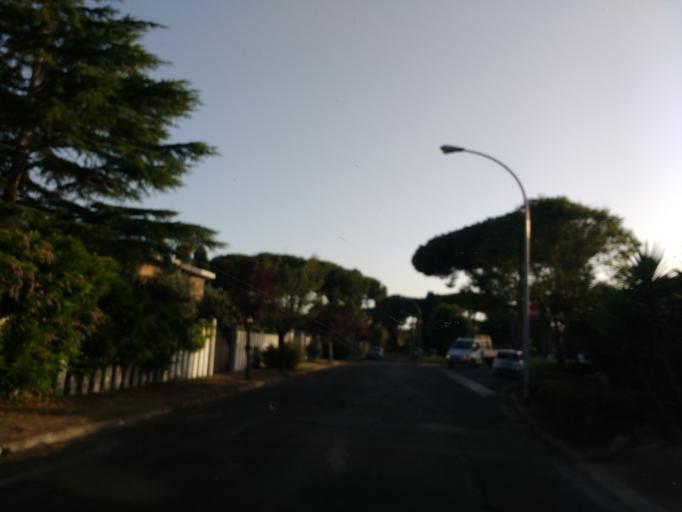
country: IT
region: Latium
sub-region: Citta metropolitana di Roma Capitale
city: Acilia-Castel Fusano-Ostia Antica
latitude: 41.7546
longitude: 12.3637
